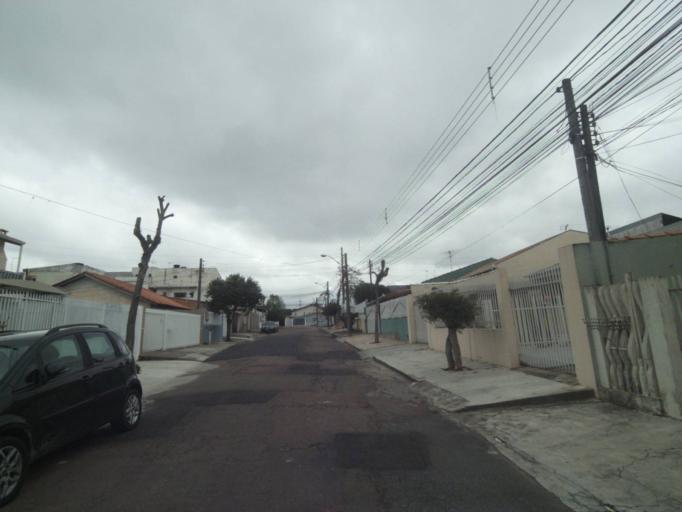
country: BR
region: Parana
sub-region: Sao Jose Dos Pinhais
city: Sao Jose dos Pinhais
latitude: -25.5415
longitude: -49.2758
